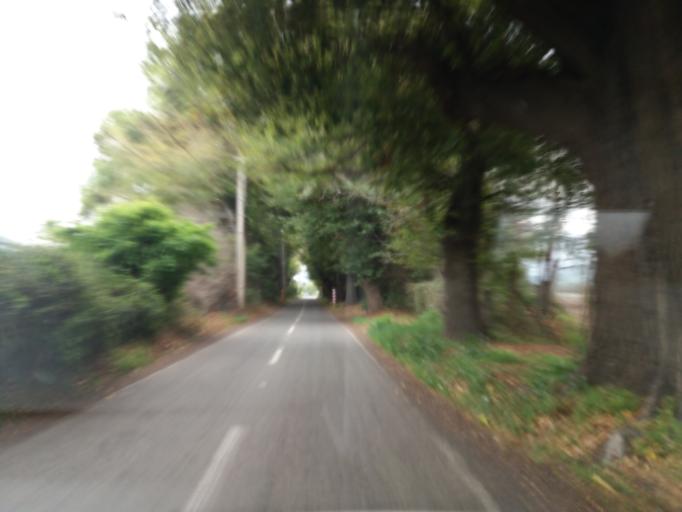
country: CL
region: Valparaiso
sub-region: Provincia de Quillota
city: Quillota
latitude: -32.8948
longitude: -71.1069
